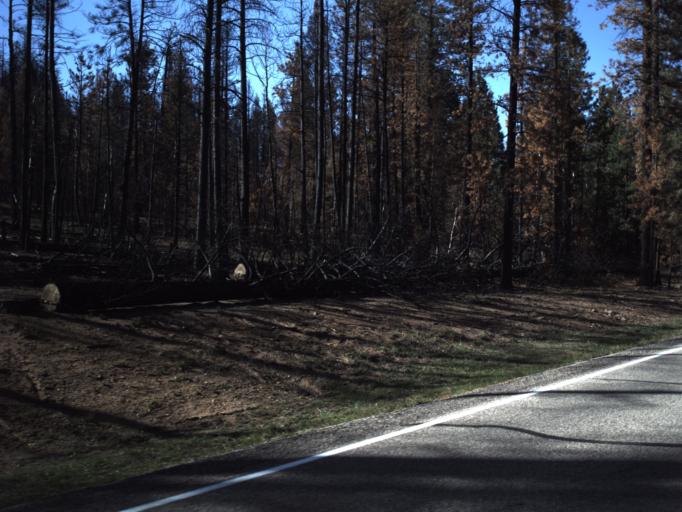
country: US
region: Utah
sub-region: Iron County
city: Parowan
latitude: 37.6629
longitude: -112.6657
